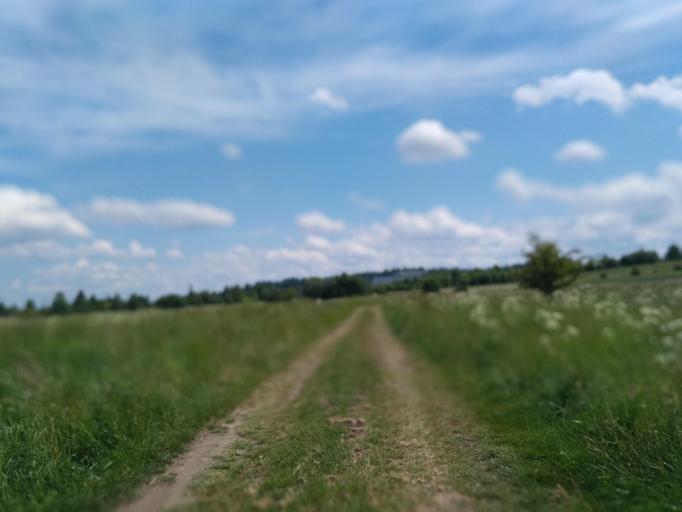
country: PL
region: Subcarpathian Voivodeship
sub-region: Powiat krosnienski
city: Odrzykon
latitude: 49.7192
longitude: 21.7474
